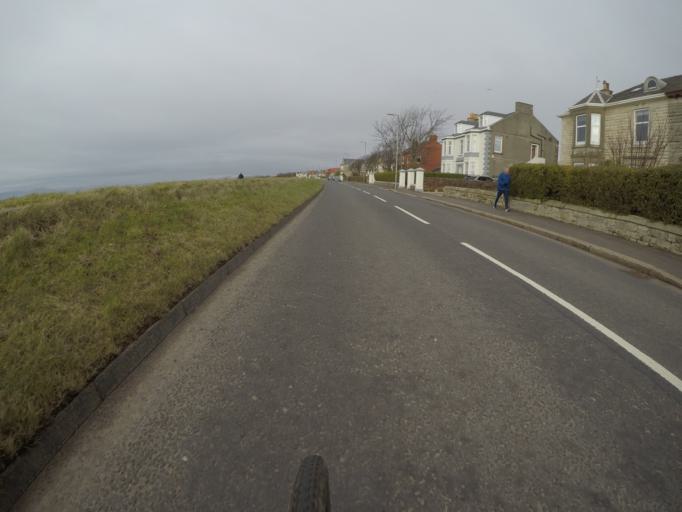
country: GB
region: Scotland
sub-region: North Ayrshire
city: Ardrossan
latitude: 55.6483
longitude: -4.8139
